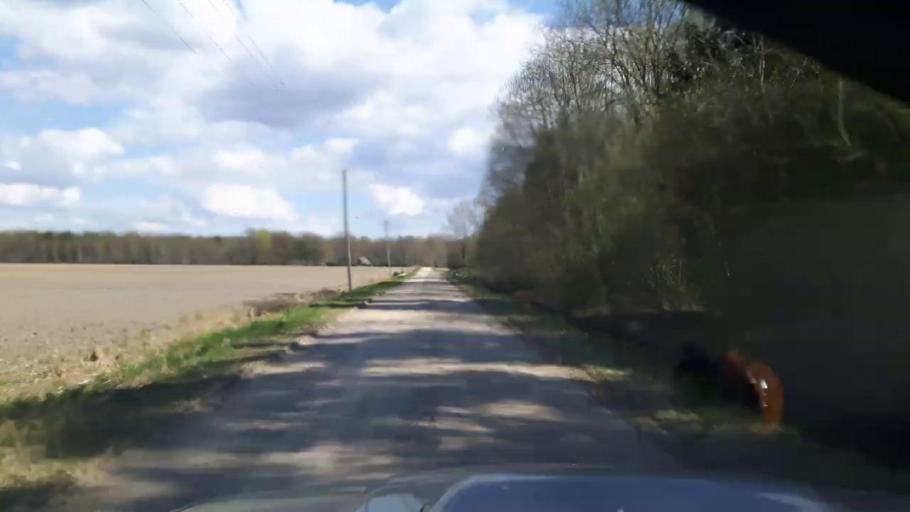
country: EE
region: Paernumaa
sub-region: Tootsi vald
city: Tootsi
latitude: 58.4572
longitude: 24.8113
